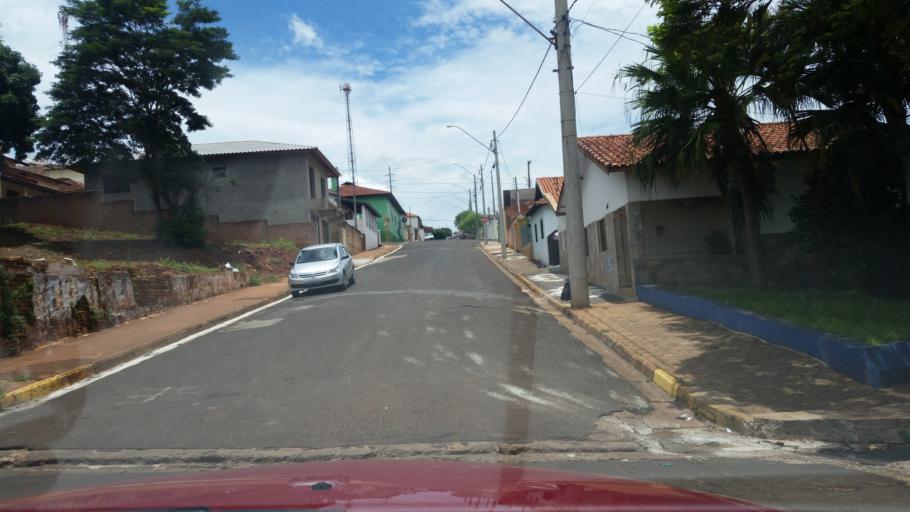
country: BR
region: Sao Paulo
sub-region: Itai
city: Itai
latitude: -23.4171
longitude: -49.0928
